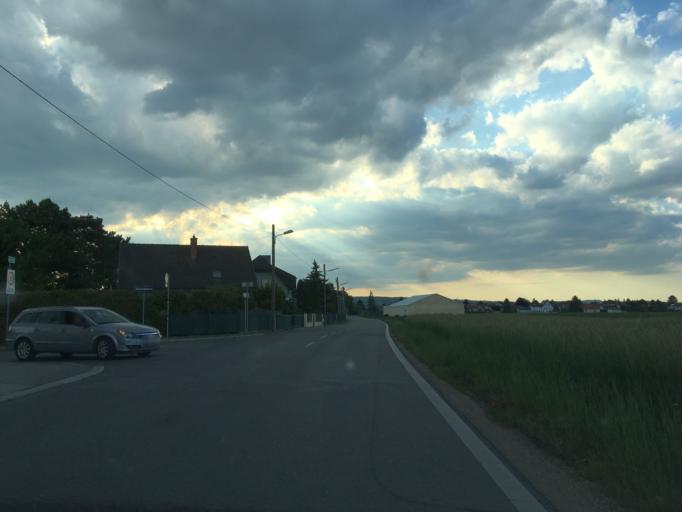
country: AT
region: Lower Austria
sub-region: Politischer Bezirk Wien-Umgebung
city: Gerasdorf bei Wien
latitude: 48.2838
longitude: 16.4574
